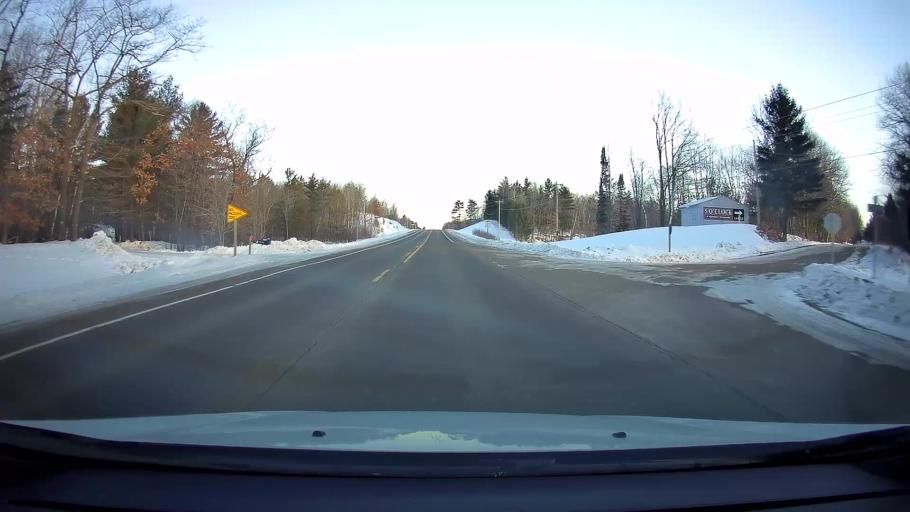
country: US
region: Wisconsin
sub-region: Barron County
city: Cumberland
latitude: 45.5819
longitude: -92.0176
